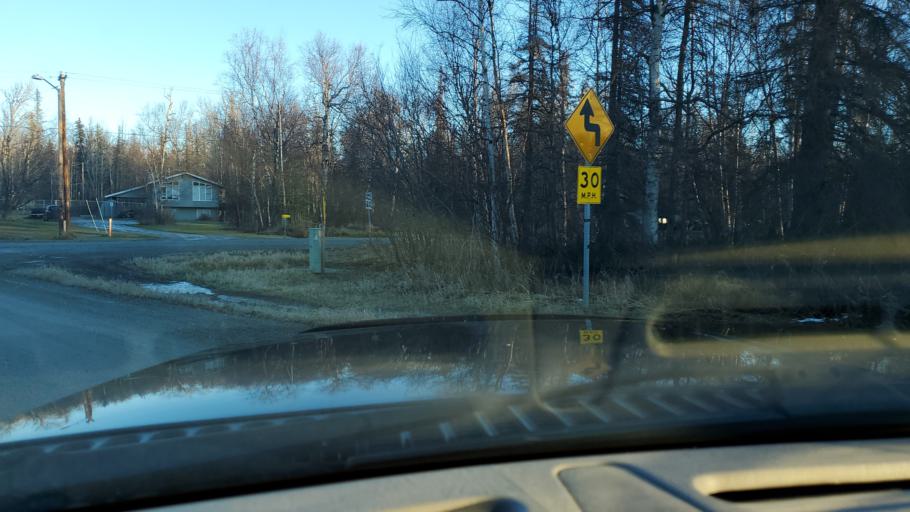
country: US
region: Alaska
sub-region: Matanuska-Susitna Borough
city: Gateway
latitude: 61.5885
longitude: -149.2465
